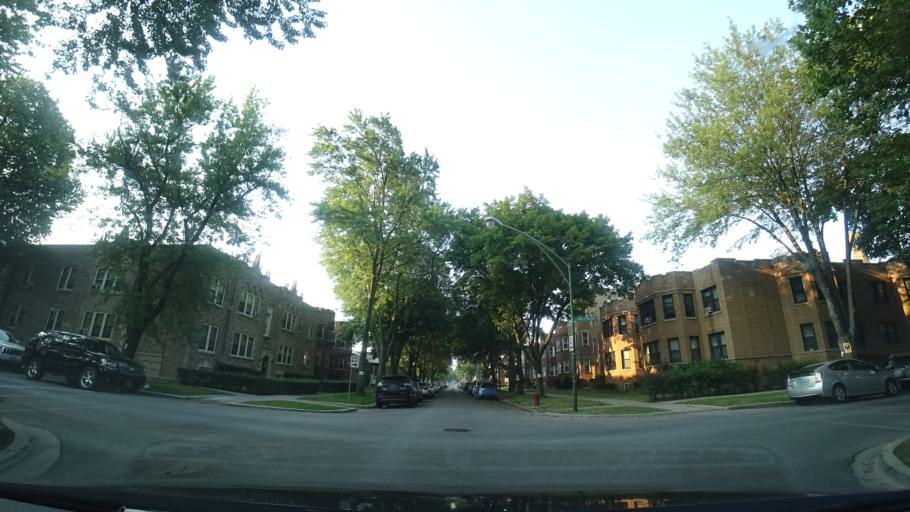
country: US
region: Illinois
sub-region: Cook County
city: Lincolnwood
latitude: 41.9852
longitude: -87.6943
